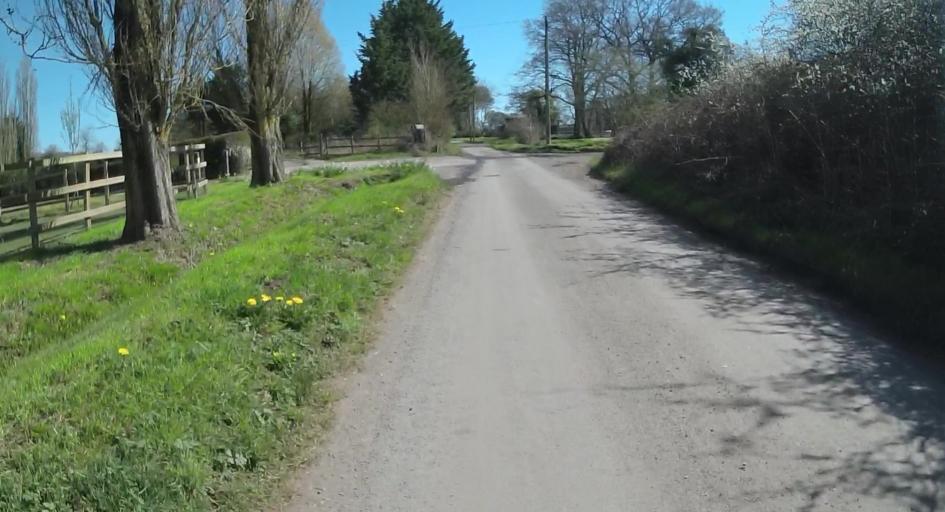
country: GB
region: England
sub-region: Hampshire
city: Odiham
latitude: 51.2487
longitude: -0.9132
